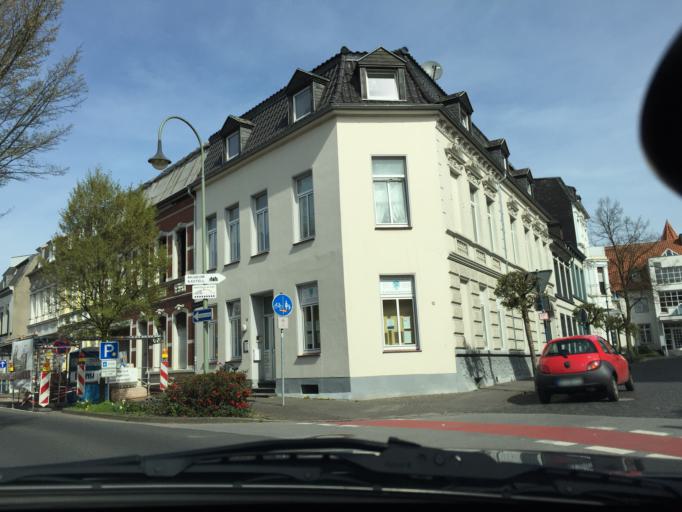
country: DE
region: North Rhine-Westphalia
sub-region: Regierungsbezirk Dusseldorf
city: Goch
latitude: 51.6746
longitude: 6.1613
